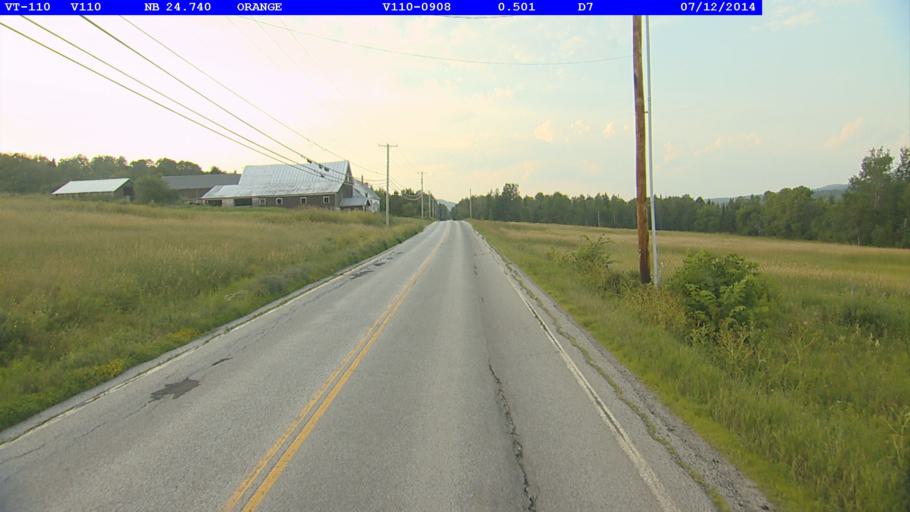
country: US
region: Vermont
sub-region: Washington County
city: South Barre
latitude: 44.1314
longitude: -72.4310
